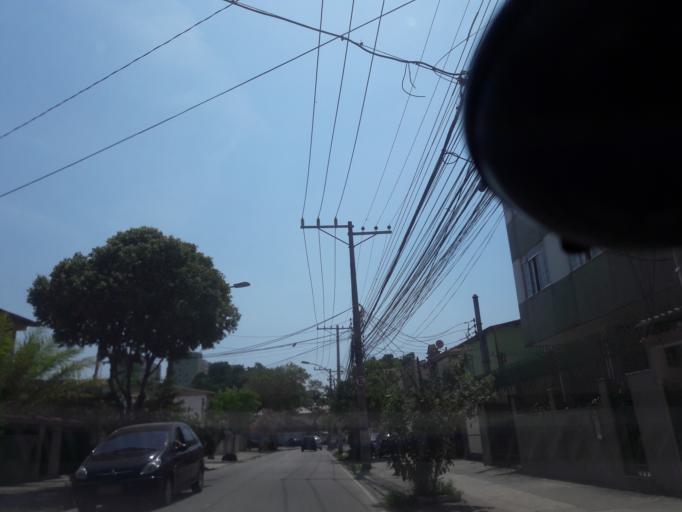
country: BR
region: Rio de Janeiro
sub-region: Sao Joao De Meriti
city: Sao Joao de Meriti
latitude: -22.8796
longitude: -43.3507
